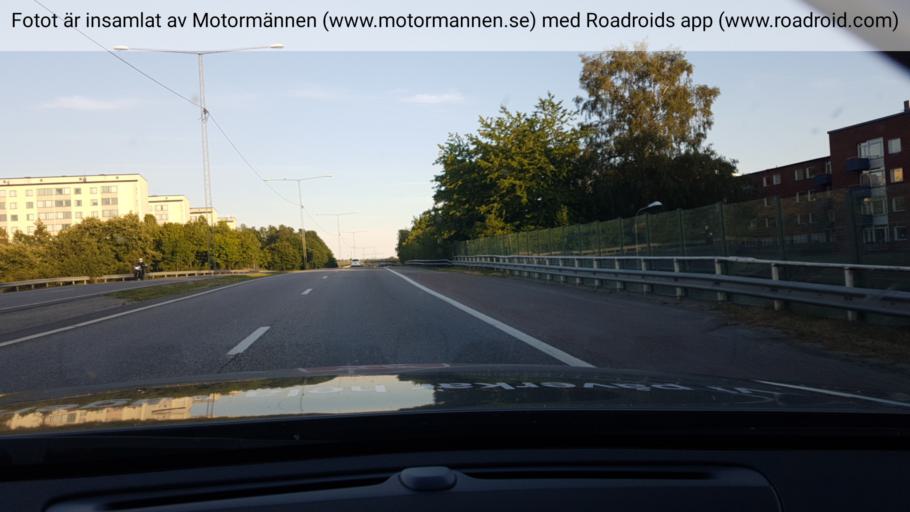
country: SE
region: Stockholm
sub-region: Huddinge Kommun
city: Huddinge
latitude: 59.2643
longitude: 18.0070
